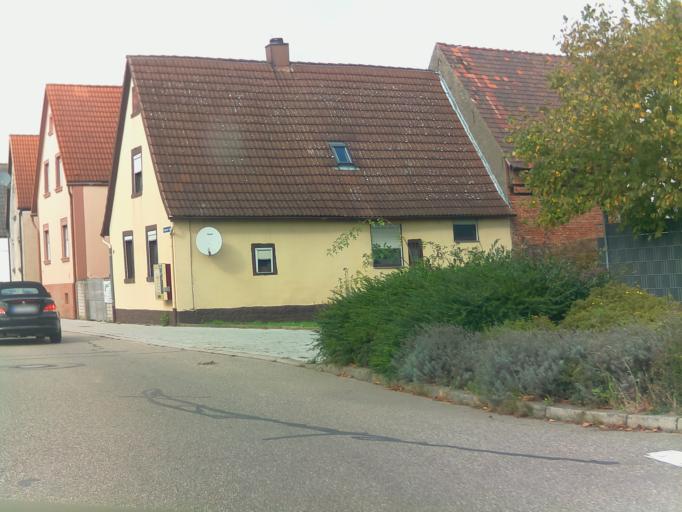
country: DE
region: Baden-Wuerttemberg
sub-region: Karlsruhe Region
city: Weingarten
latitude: 49.0894
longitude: 8.5121
